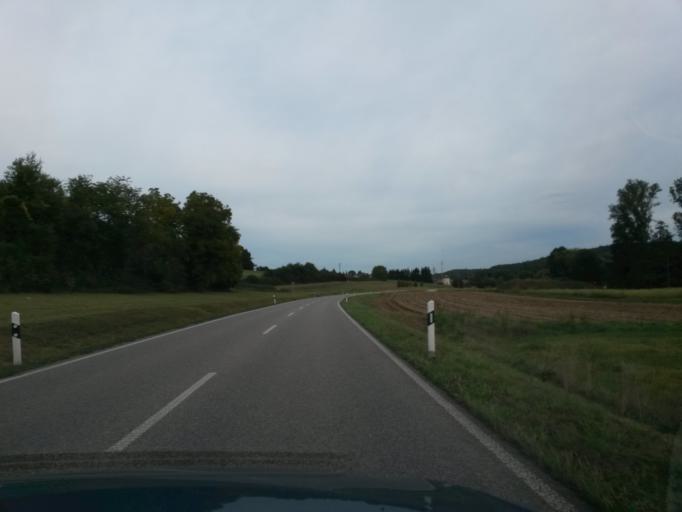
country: DE
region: Baden-Wuerttemberg
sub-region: Karlsruhe Region
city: Konigsbach-Stein
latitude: 48.9205
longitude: 8.5610
